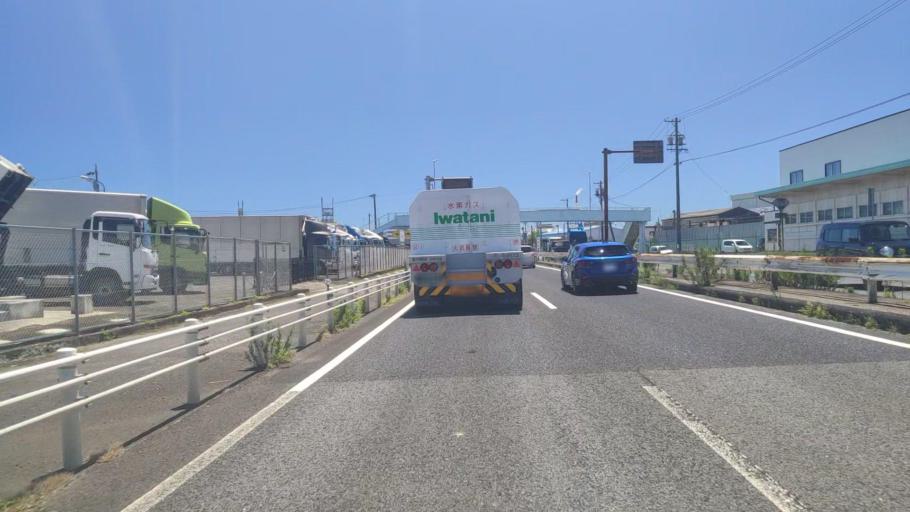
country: JP
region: Mie
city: Yokkaichi
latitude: 34.9445
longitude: 136.6190
